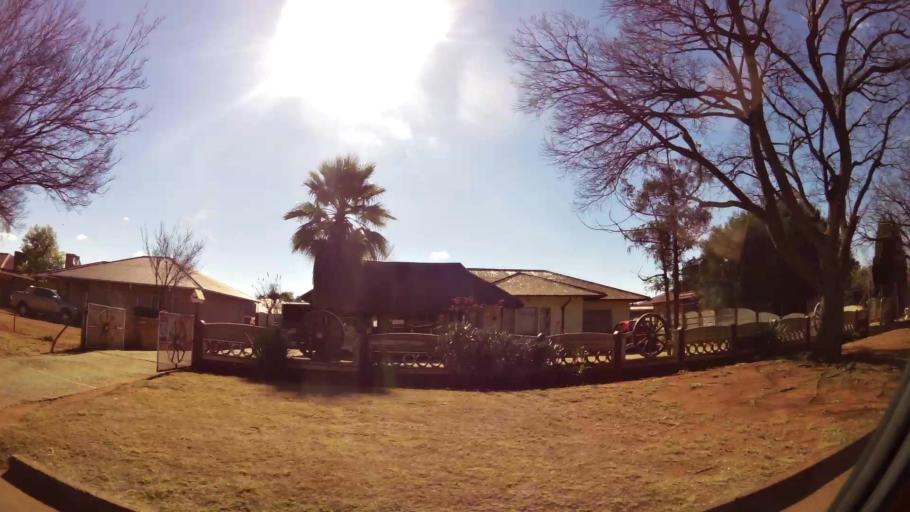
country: ZA
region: Gauteng
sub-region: West Rand District Municipality
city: Carletonville
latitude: -26.3566
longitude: 27.3890
